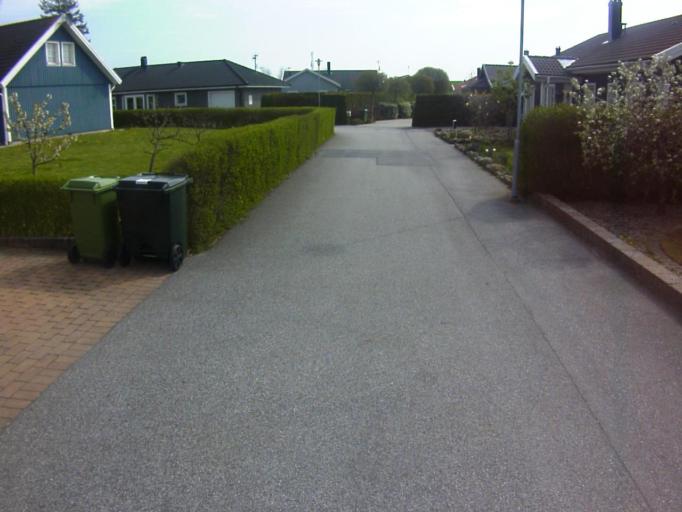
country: SE
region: Skane
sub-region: Kavlinge Kommun
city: Loddekopinge
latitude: 55.8179
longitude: 13.0227
